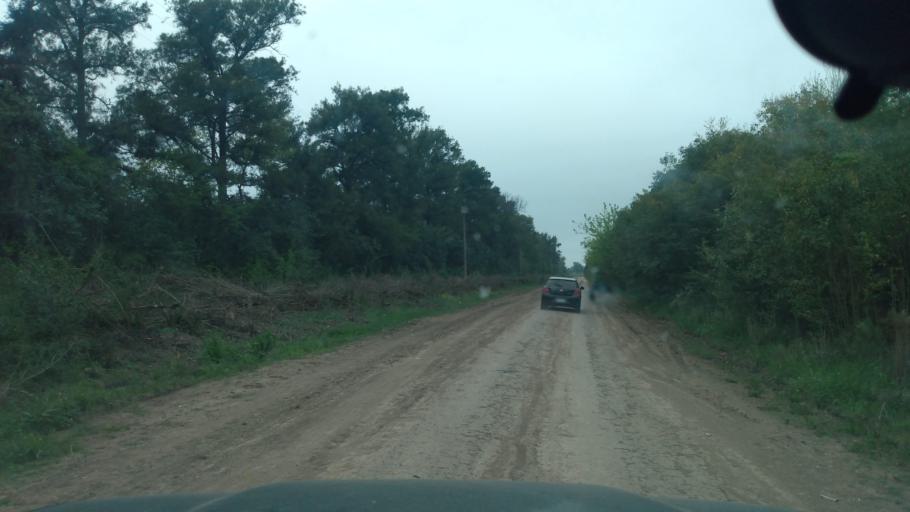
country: AR
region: Buenos Aires
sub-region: Partido de Lujan
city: Lujan
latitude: -34.5402
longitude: -59.2055
